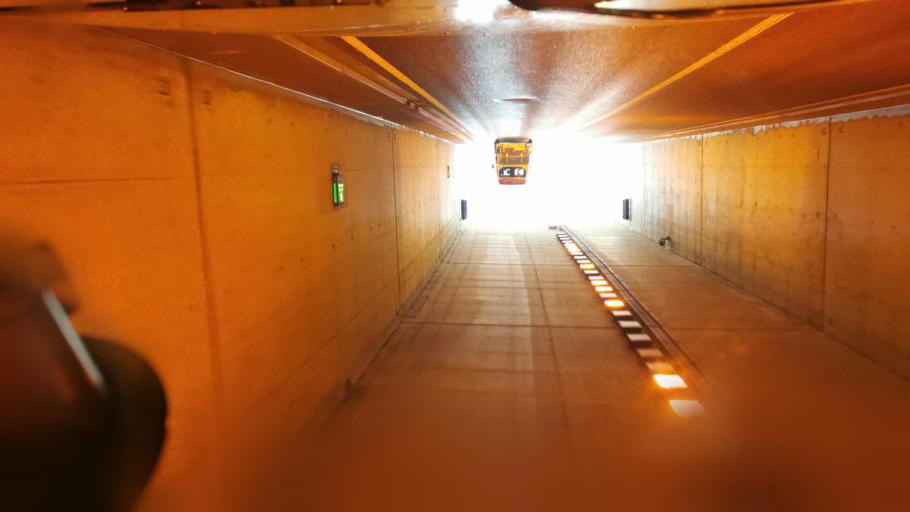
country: DE
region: Baden-Wuerttemberg
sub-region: Regierungsbezirk Stuttgart
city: Donzdorf
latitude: 48.6963
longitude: 9.8098
